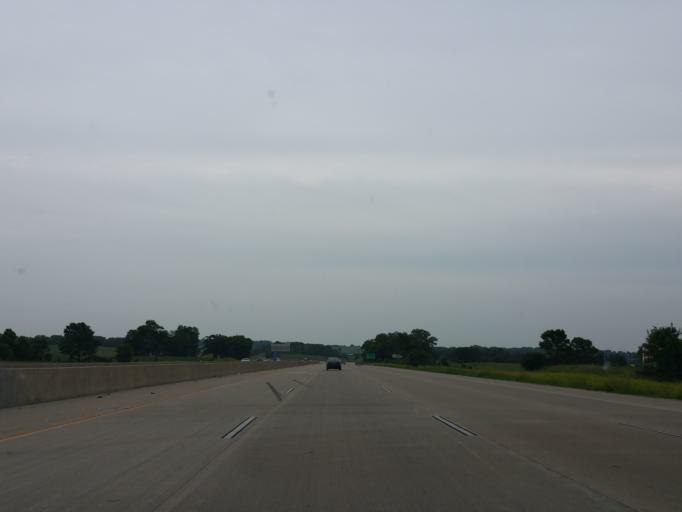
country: US
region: Wisconsin
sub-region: Dane County
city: Cottage Grove
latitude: 43.1034
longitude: -89.2640
